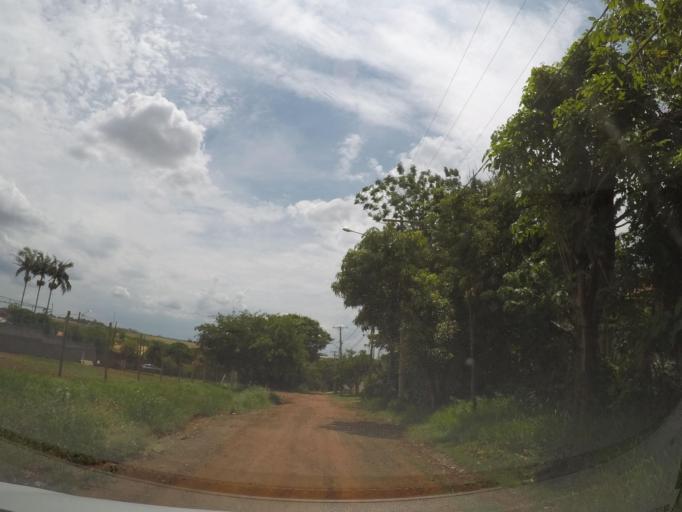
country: BR
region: Sao Paulo
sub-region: Sumare
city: Sumare
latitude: -22.8481
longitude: -47.2985
